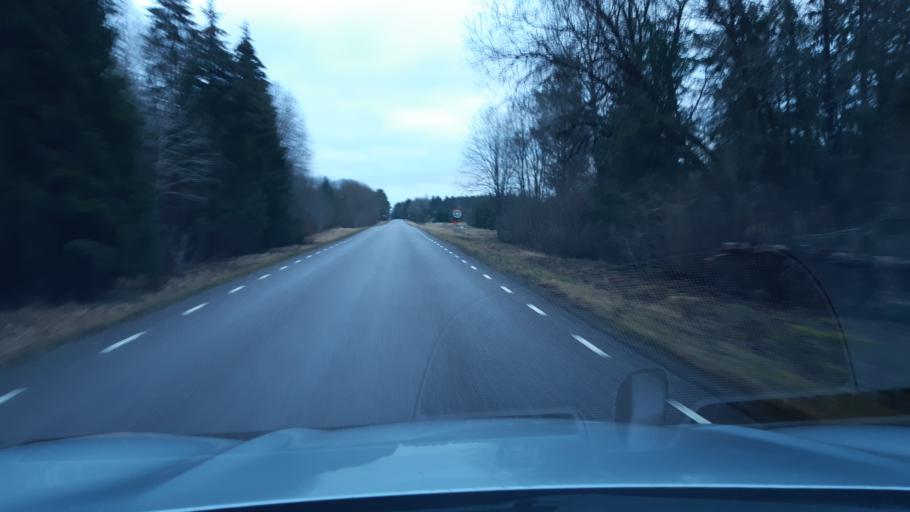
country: EE
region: Raplamaa
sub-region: Kohila vald
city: Kohila
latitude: 59.1304
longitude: 24.6661
